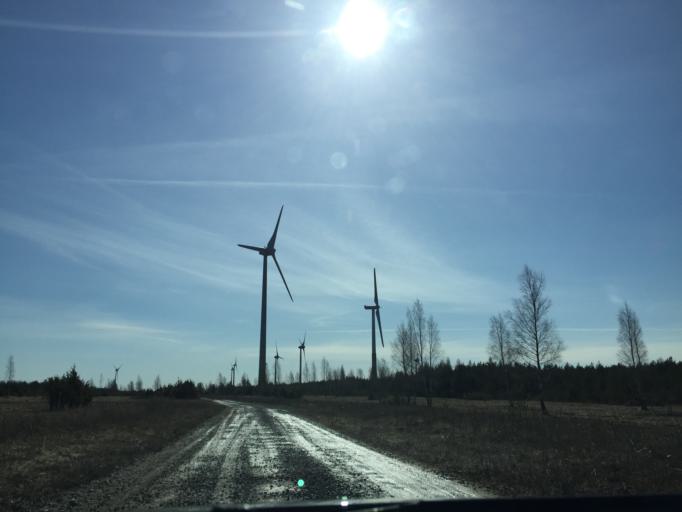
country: EE
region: Laeaene
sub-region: Haapsalu linn
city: Haapsalu
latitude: 58.6310
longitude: 23.5266
